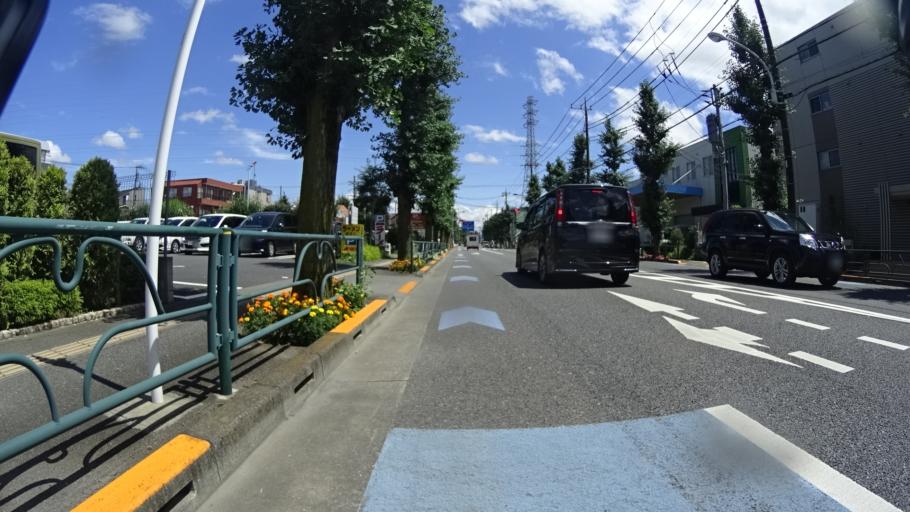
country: JP
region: Tokyo
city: Fussa
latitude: 35.7753
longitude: 139.2993
